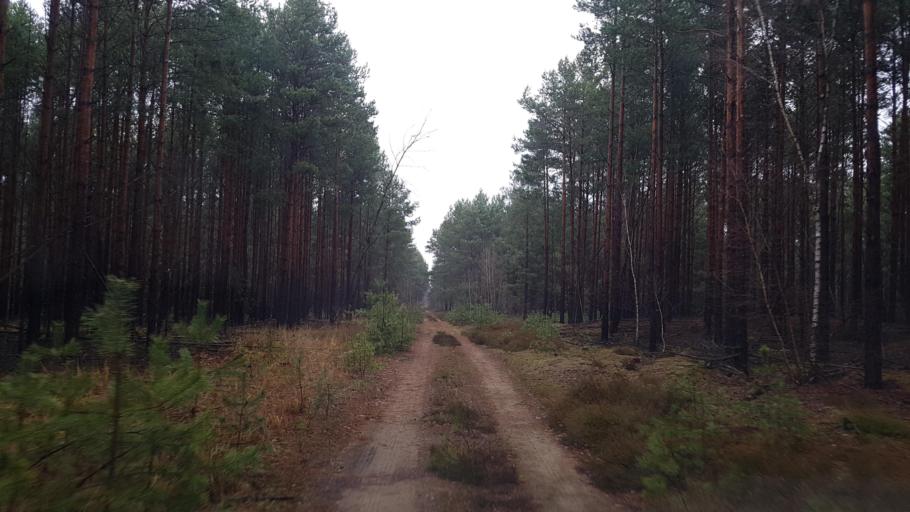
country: DE
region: Brandenburg
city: Grossraschen
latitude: 51.6268
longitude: 13.9685
